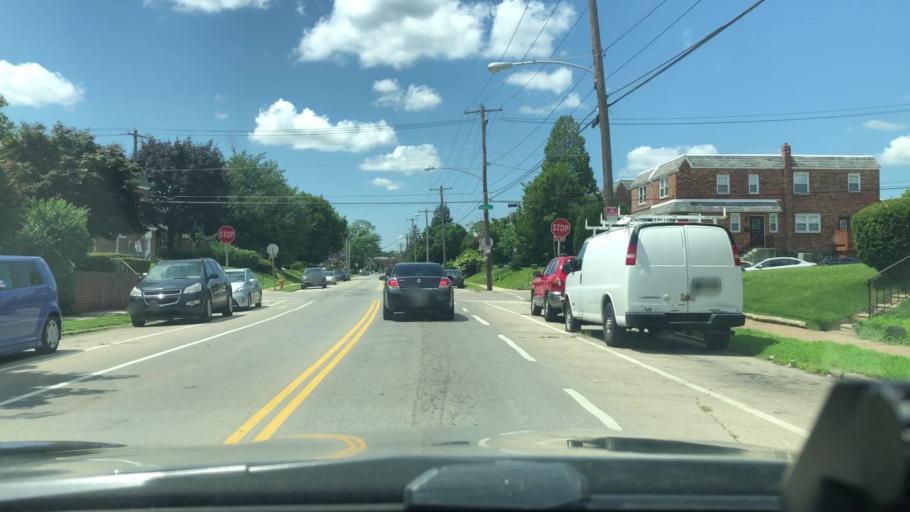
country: US
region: Pennsylvania
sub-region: Montgomery County
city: Wyndmoor
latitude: 40.0673
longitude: -75.1740
